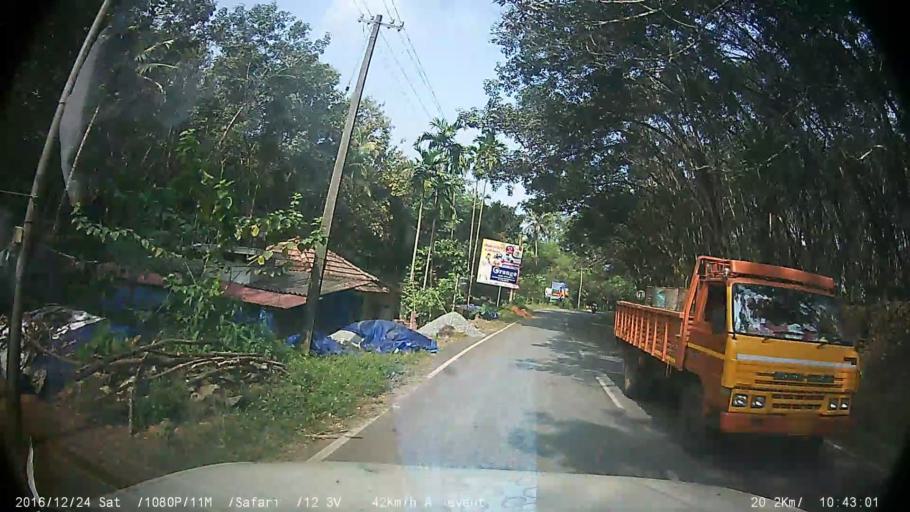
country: IN
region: Kerala
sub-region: Ernakulam
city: Muvattupuzha
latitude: 9.8829
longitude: 76.5996
